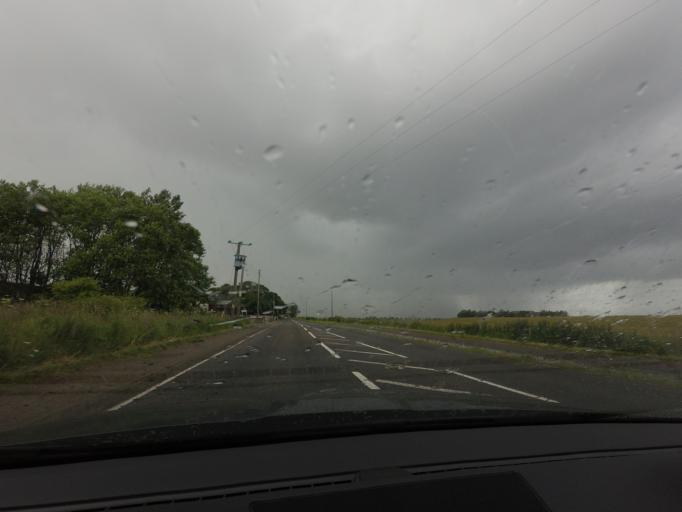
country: GB
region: Scotland
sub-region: Moray
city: Buckie
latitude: 57.6601
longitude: -2.9694
